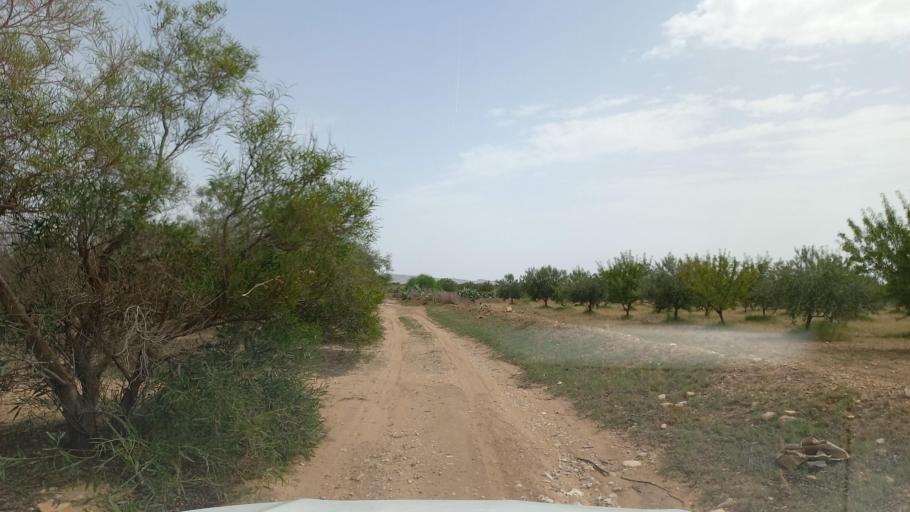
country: TN
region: Al Qasrayn
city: Kasserine
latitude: 35.2930
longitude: 9.0135
